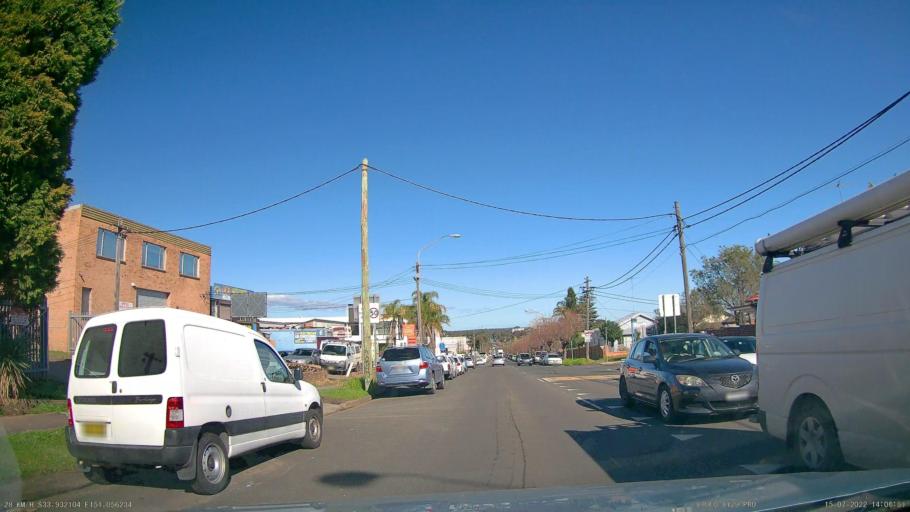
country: AU
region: New South Wales
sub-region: Canterbury
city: Roselands
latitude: -33.9322
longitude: 151.0562
